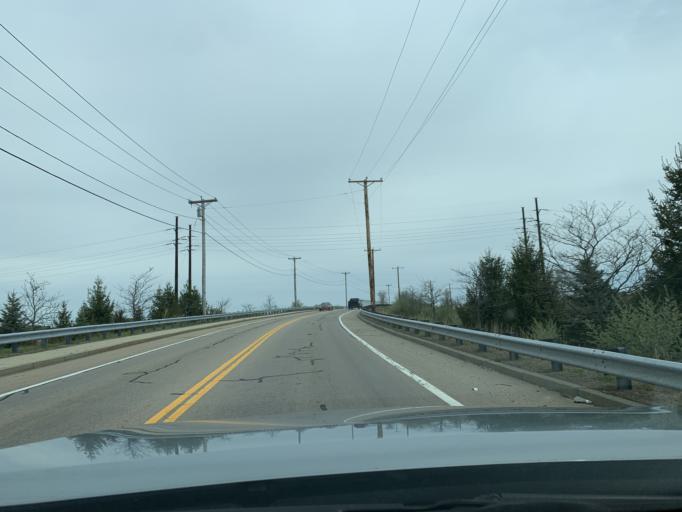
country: US
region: Rhode Island
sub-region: Kent County
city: East Greenwich
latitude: 41.6066
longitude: -71.4735
